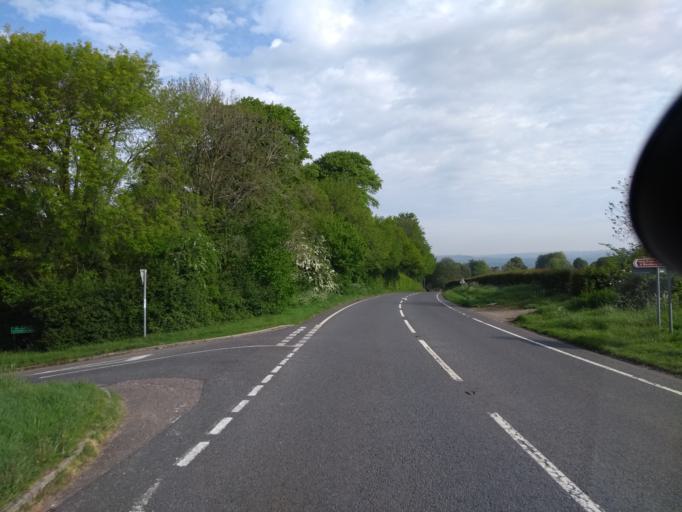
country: GB
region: England
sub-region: Devon
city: Axminster
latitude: 50.7692
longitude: -2.9788
